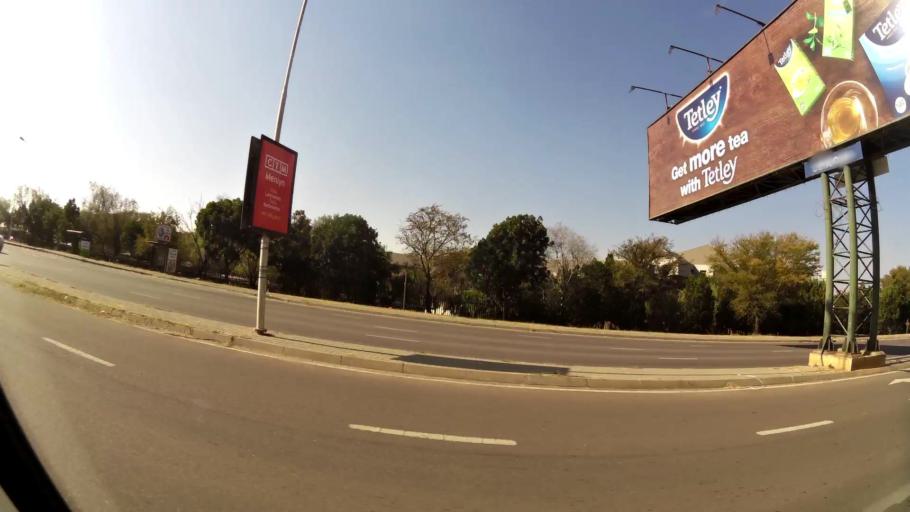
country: ZA
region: Gauteng
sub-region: City of Tshwane Metropolitan Municipality
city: Pretoria
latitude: -25.7868
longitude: 28.2736
